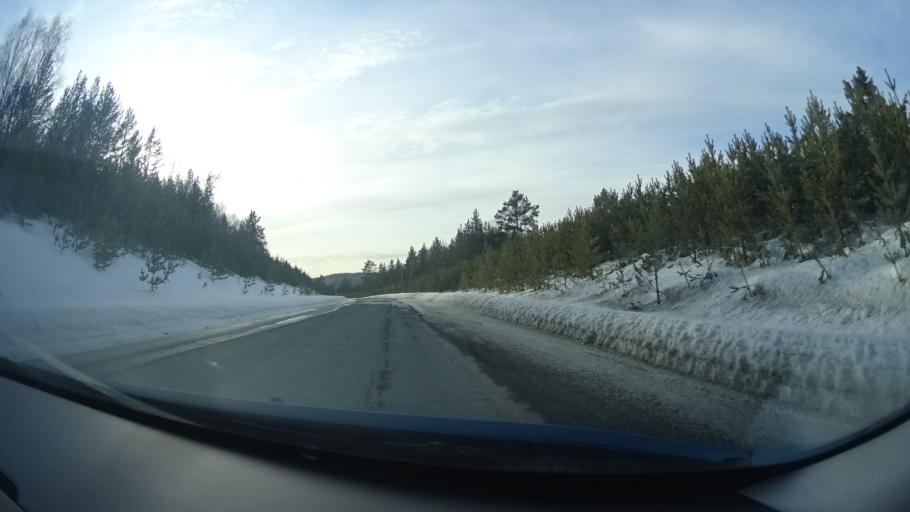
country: RU
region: Bashkortostan
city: Lomovka
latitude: 53.6719
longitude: 58.2346
